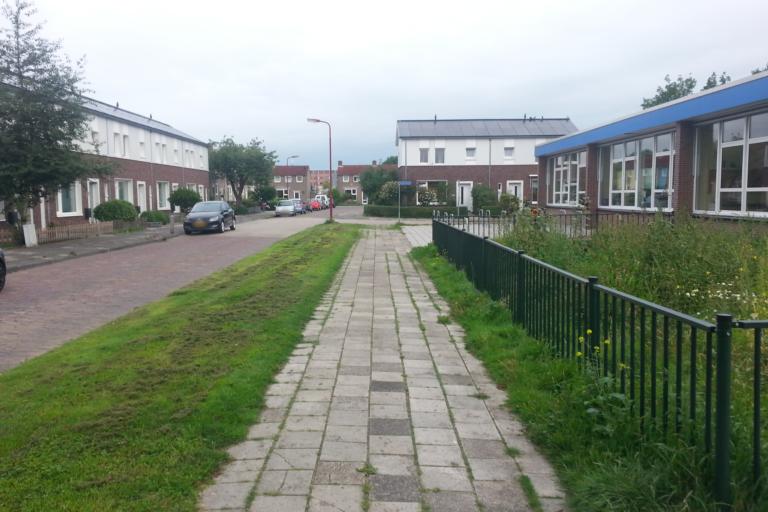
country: NL
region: Friesland
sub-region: Gemeente Heerenveen
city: Heerenveen
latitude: 52.9577
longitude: 5.9215
